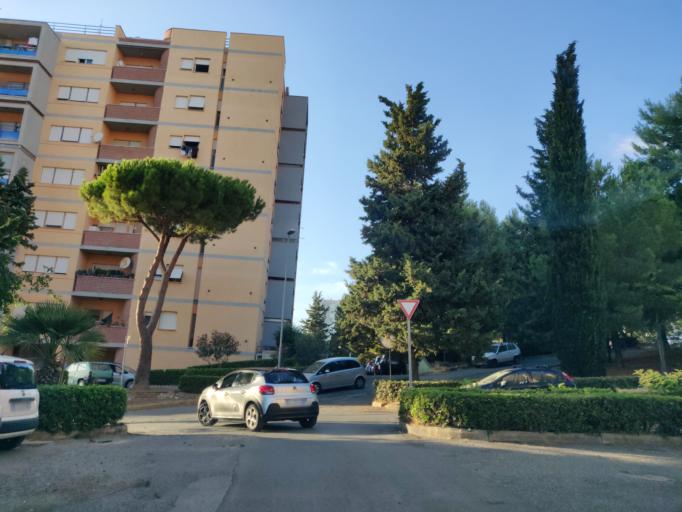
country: IT
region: Latium
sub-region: Citta metropolitana di Roma Capitale
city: Civitavecchia
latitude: 42.0944
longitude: 11.8174
